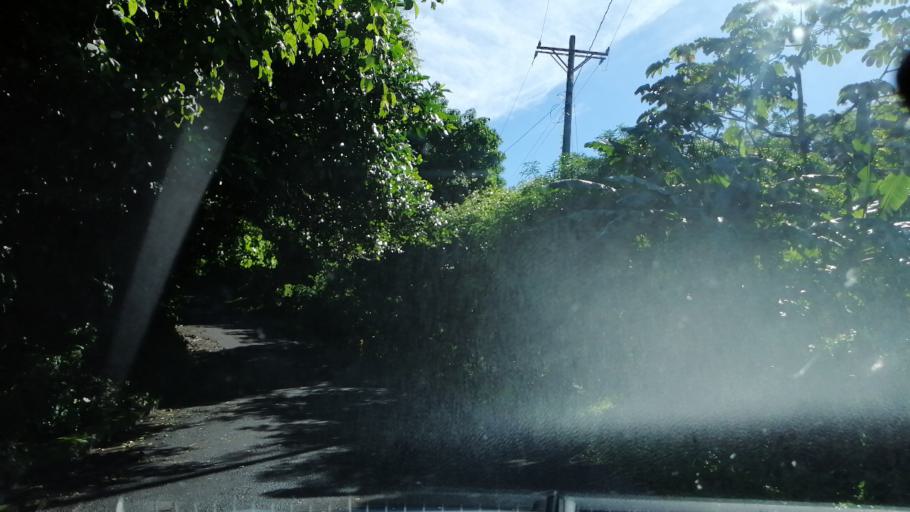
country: SV
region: Morazan
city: Cacaopera
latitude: 13.7808
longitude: -88.0359
